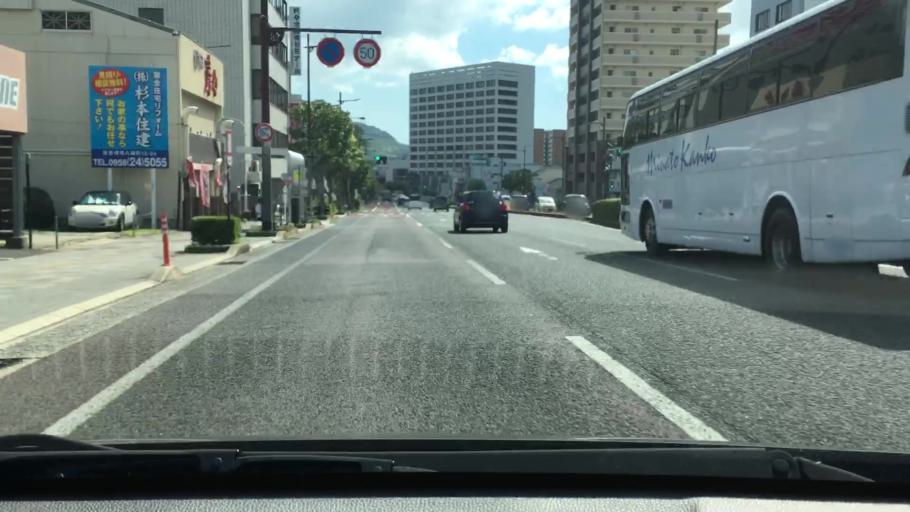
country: JP
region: Nagasaki
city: Sasebo
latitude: 33.1832
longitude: 129.7174
